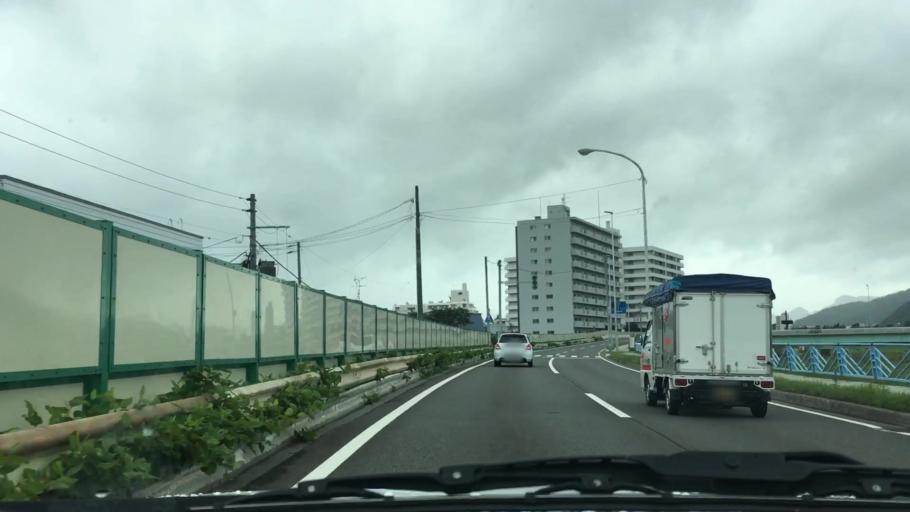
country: JP
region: Hokkaido
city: Sapporo
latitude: 43.0312
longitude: 141.3572
